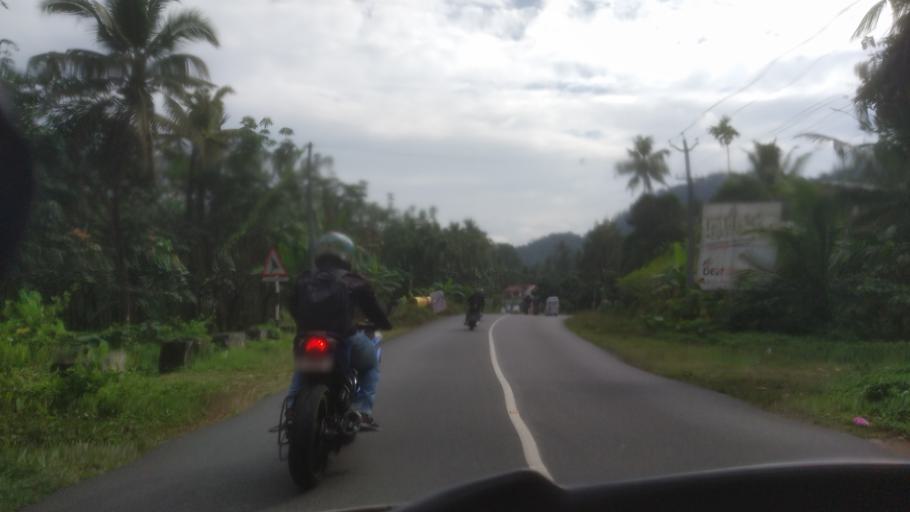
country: IN
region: Kerala
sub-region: Idukki
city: Kuttampuzha
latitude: 10.0503
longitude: 76.7521
